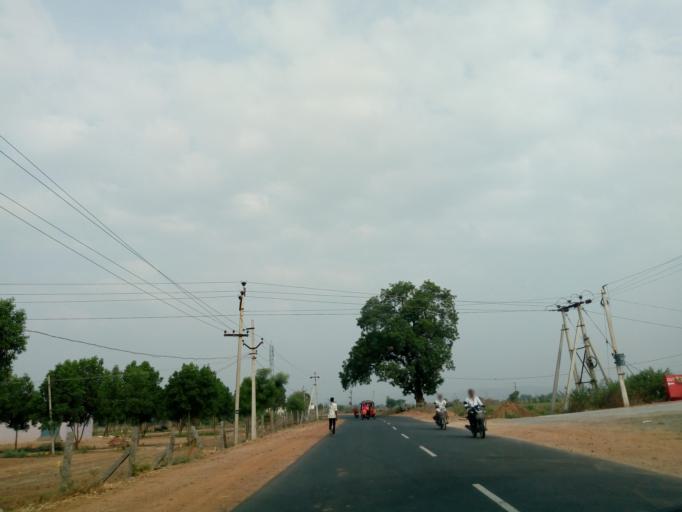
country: IN
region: Andhra Pradesh
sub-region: Prakasam
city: Diguvametta
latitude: 15.3735
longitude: 78.8777
